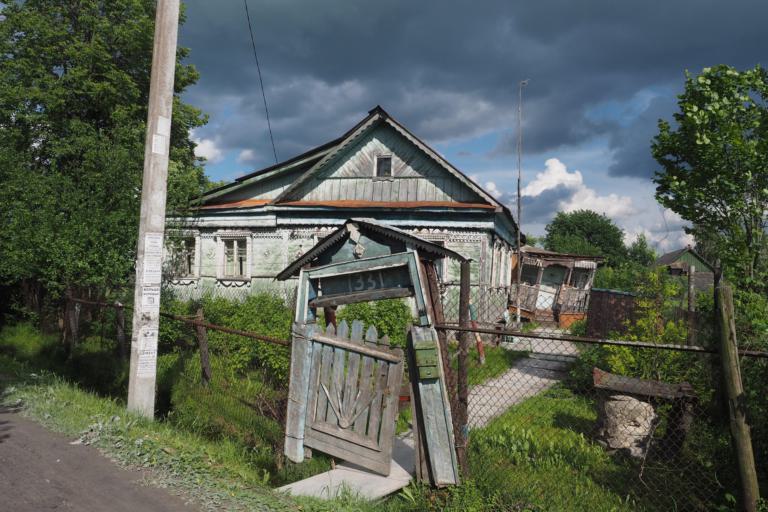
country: RU
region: Moskovskaya
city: Konobeyevo
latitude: 55.4072
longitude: 38.6704
